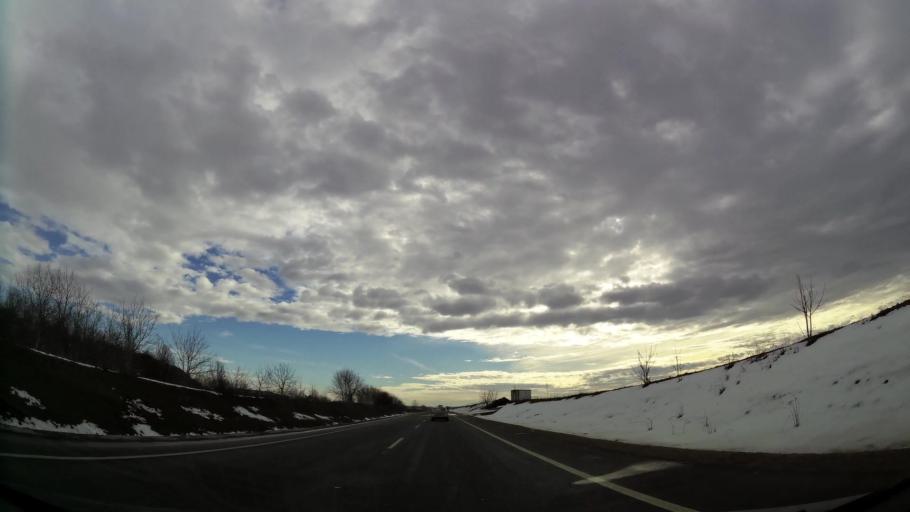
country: RS
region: Central Serbia
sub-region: Belgrade
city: Surcin
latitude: 44.8102
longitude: 20.2977
